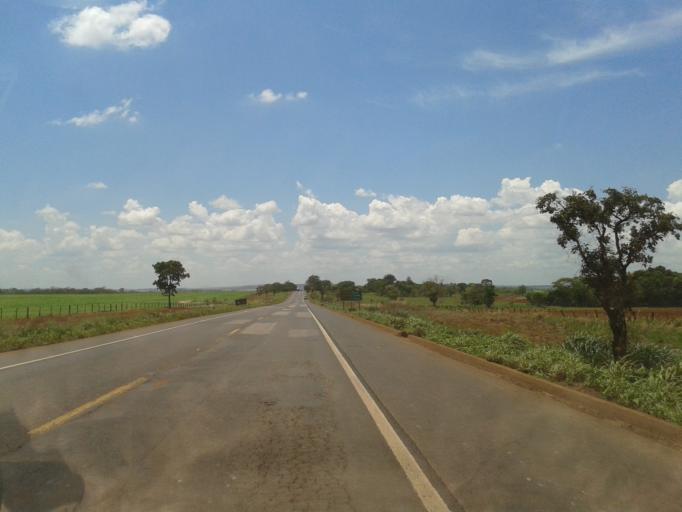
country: BR
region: Goias
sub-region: Goiatuba
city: Goiatuba
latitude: -18.2841
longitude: -49.6152
